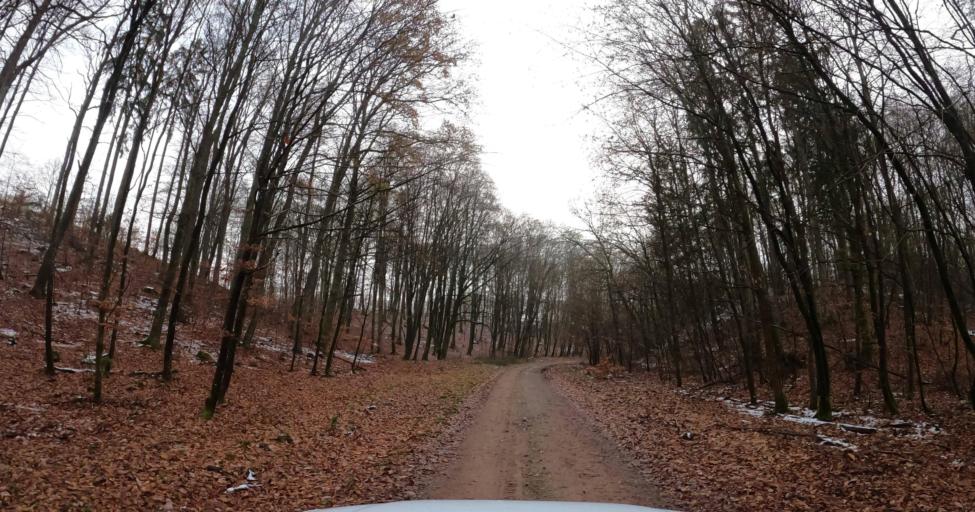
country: PL
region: West Pomeranian Voivodeship
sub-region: Powiat swidwinski
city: Rabino
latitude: 53.8923
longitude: 15.8918
